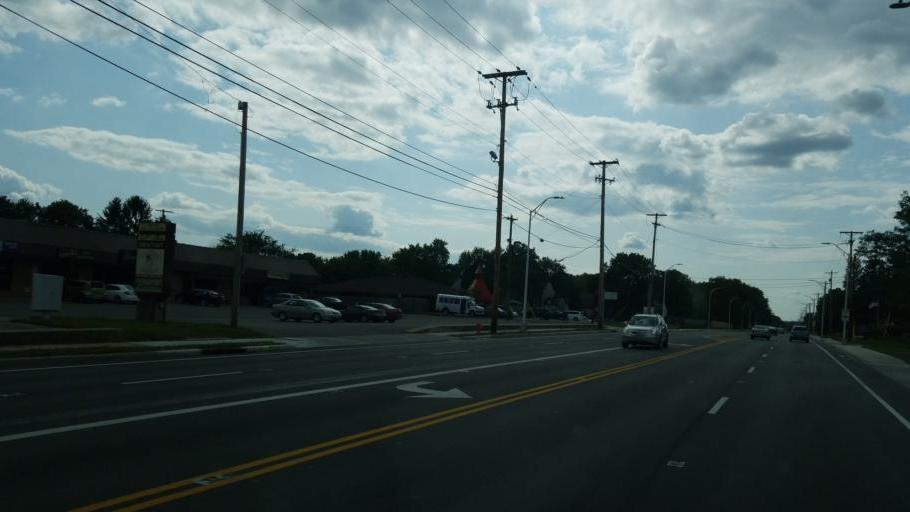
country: US
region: Ohio
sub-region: Delaware County
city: Powell
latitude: 40.1174
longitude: -83.0679
